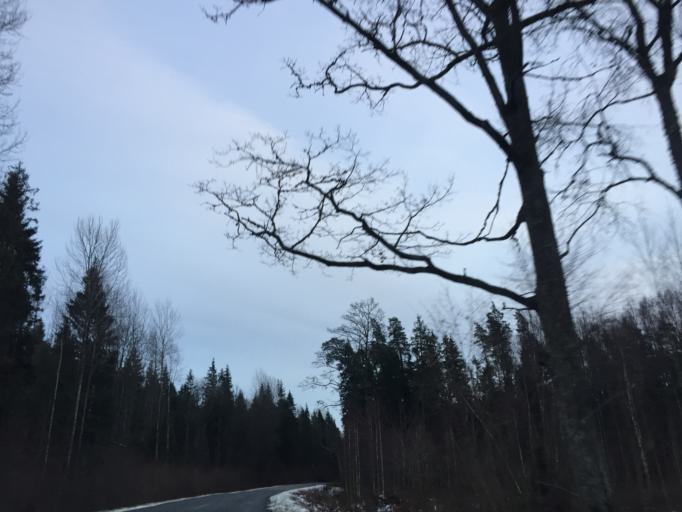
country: LV
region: Burtnieki
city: Matisi
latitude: 57.6434
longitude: 25.0336
